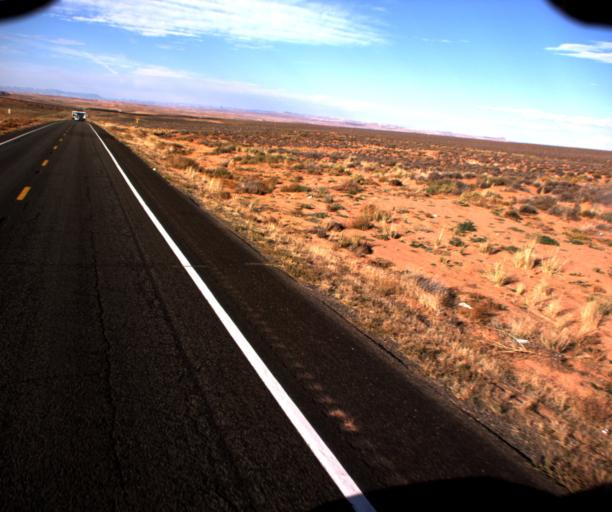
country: US
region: Arizona
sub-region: Apache County
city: Many Farms
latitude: 36.9393
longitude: -109.5498
